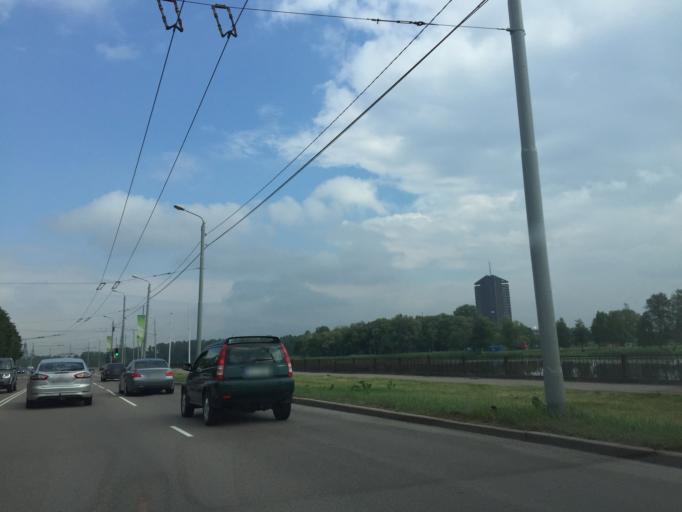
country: LV
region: Riga
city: Riga
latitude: 56.9295
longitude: 24.1071
